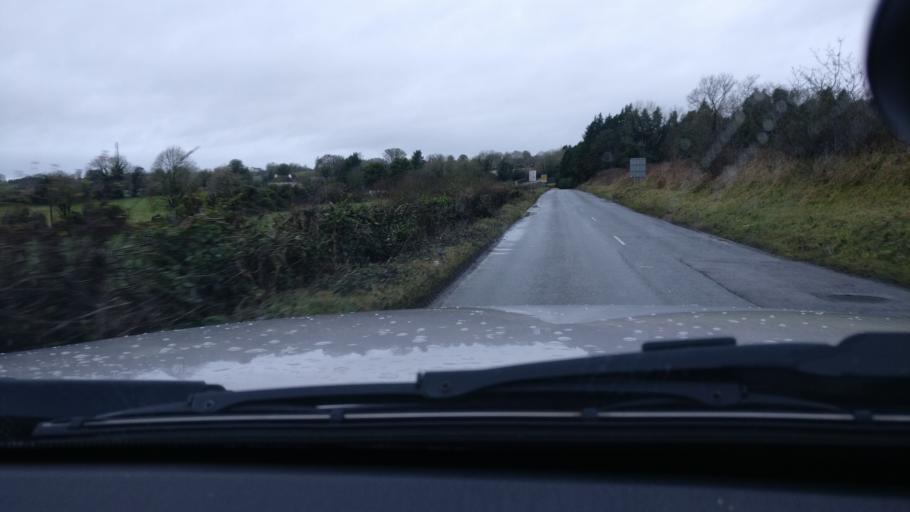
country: IE
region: Leinster
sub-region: An Longfort
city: Granard
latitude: 53.7931
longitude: -7.3993
